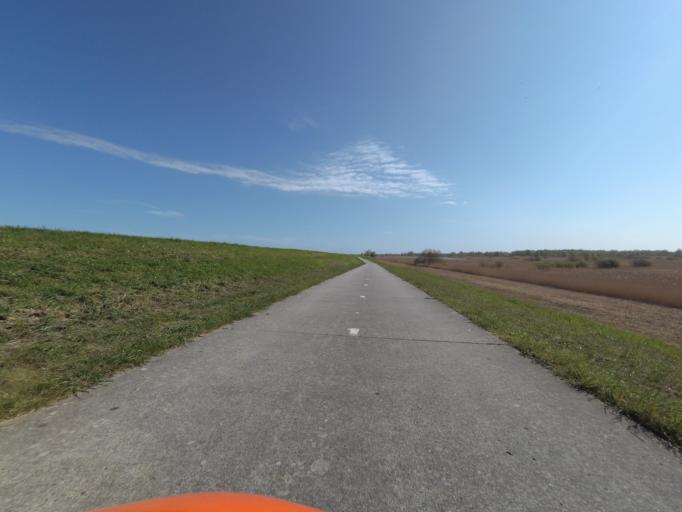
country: NL
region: Flevoland
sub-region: Gemeente Almere
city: Almere Stad
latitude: 52.4106
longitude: 5.1927
